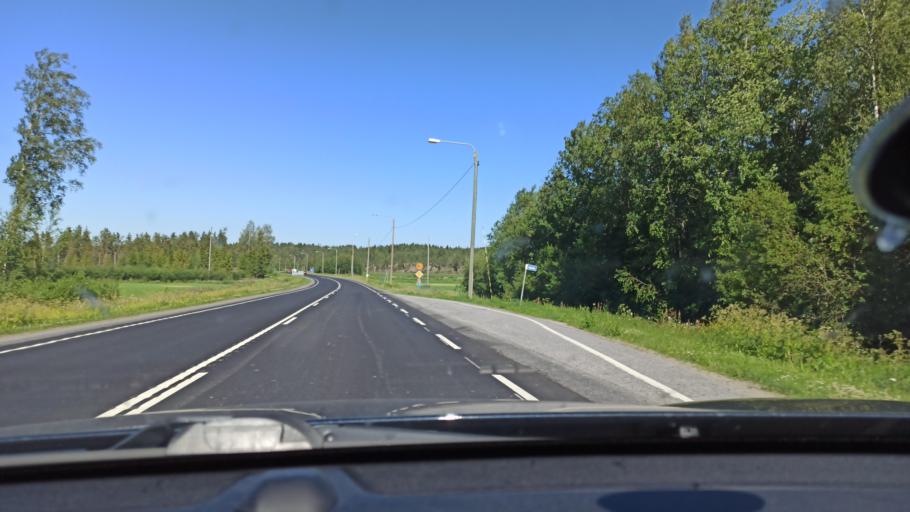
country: FI
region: Ostrobothnia
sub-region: Vaasa
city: Oravais
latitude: 63.2840
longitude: 22.3603
